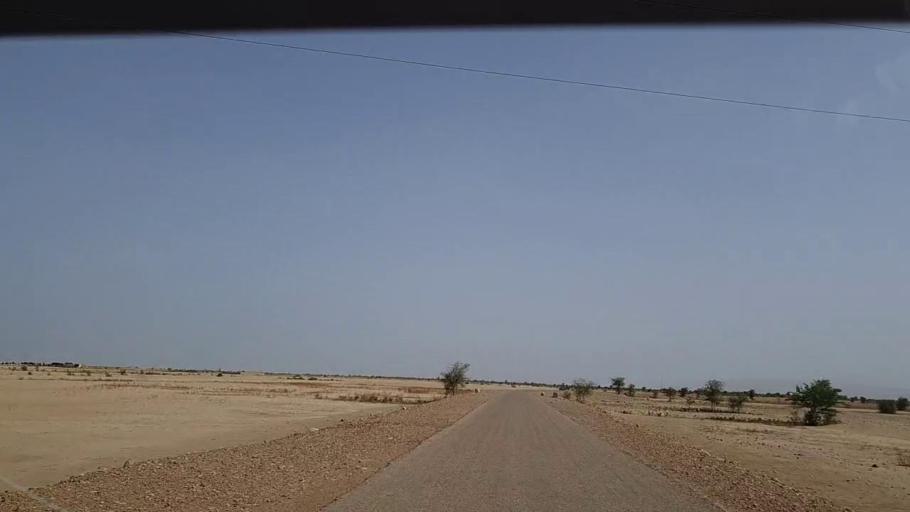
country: PK
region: Sindh
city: Johi
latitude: 26.6686
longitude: 67.5086
